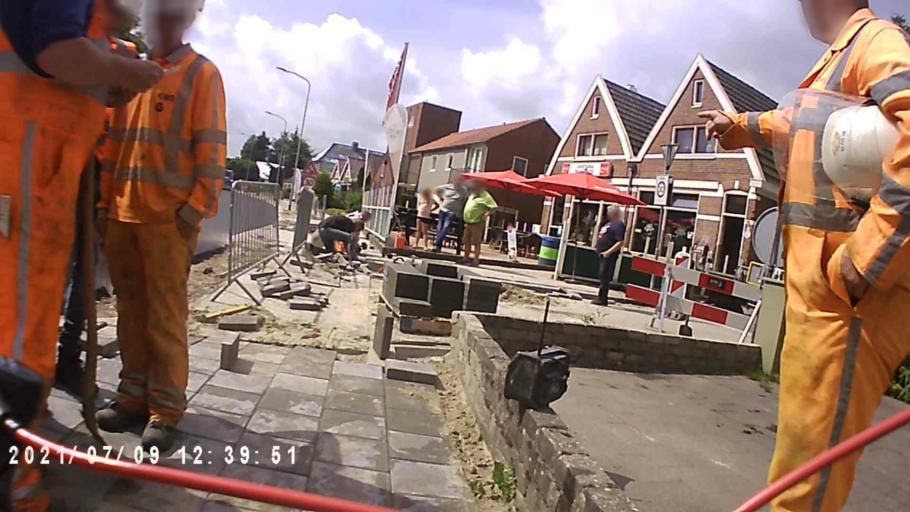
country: NL
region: Groningen
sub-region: Gemeente  Oldambt
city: Winschoten
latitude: 53.1406
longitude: 7.0210
